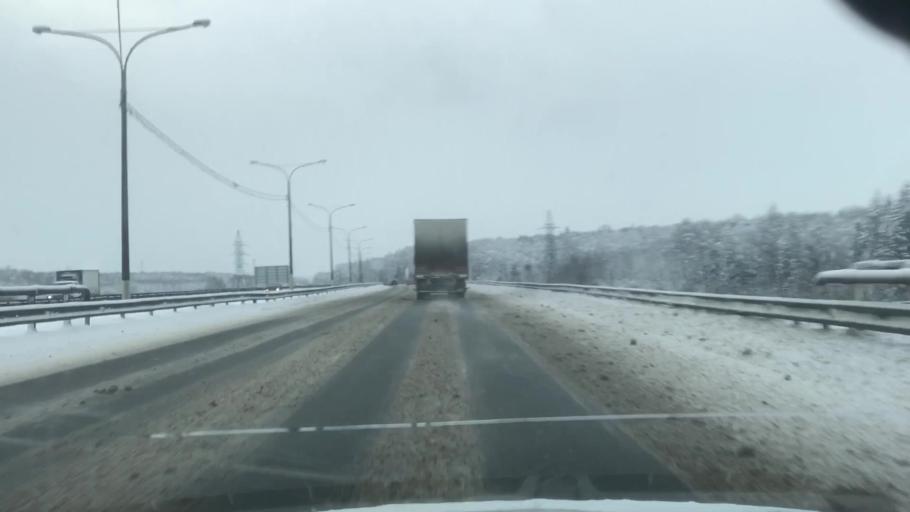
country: RU
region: Moskovskaya
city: Mikhnevo
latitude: 55.1431
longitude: 37.9314
